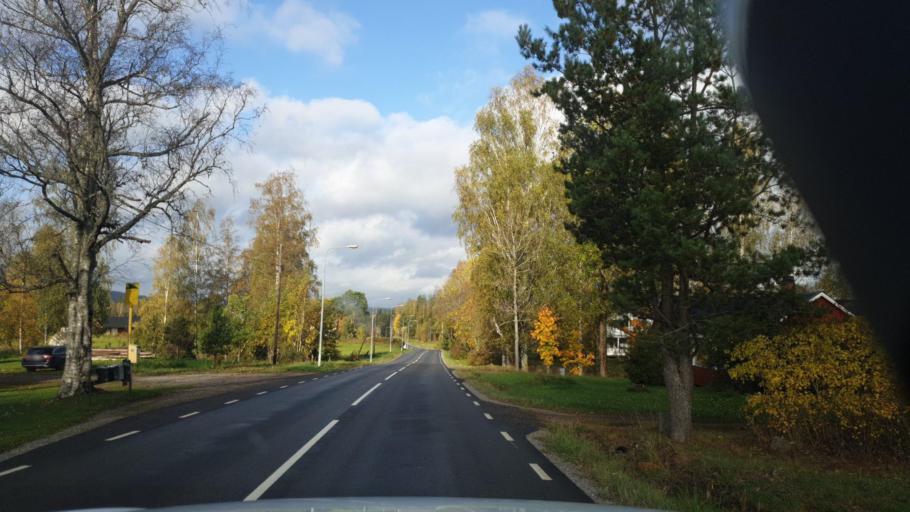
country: SE
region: Vaermland
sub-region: Arvika Kommun
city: Arvika
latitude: 59.5405
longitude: 12.5838
